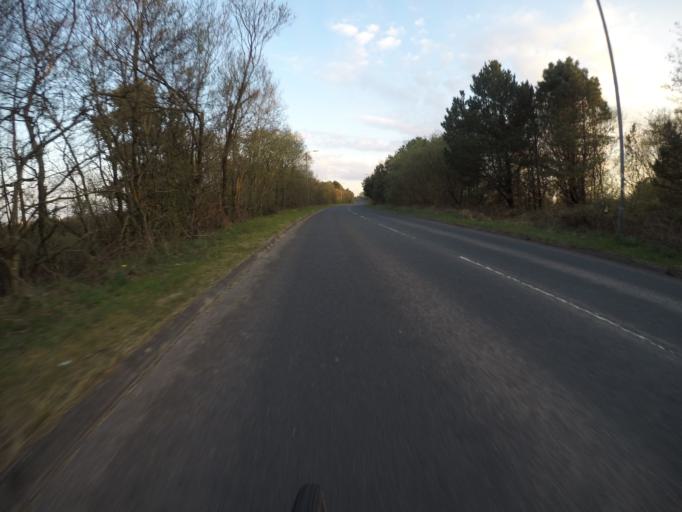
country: GB
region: Scotland
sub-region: North Ayrshire
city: Irvine
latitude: 55.5932
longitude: -4.6679
